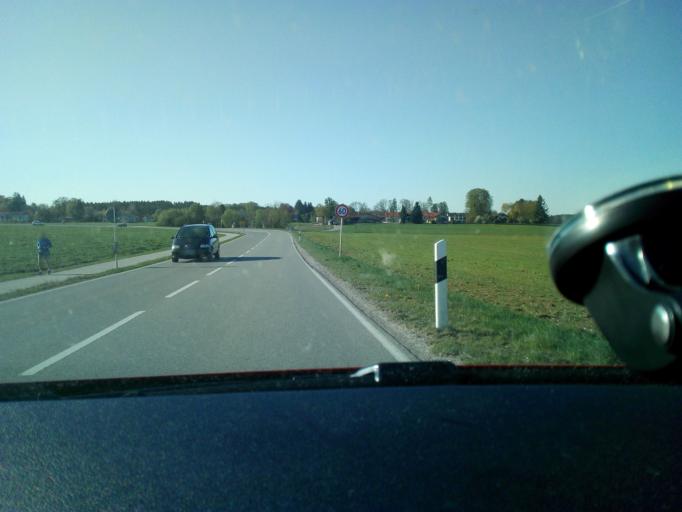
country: DE
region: Bavaria
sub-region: Upper Bavaria
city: Holzkirchen
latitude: 47.8917
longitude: 11.7025
